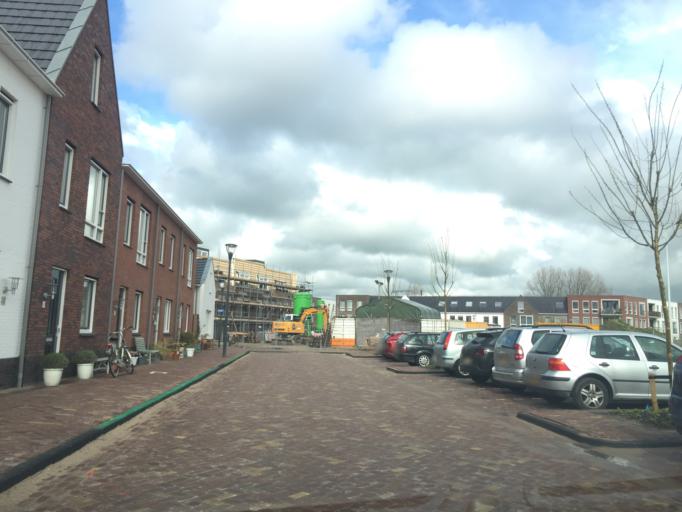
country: NL
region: South Holland
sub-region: Gemeente Leiden
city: Leiden
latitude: 52.1700
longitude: 4.4930
